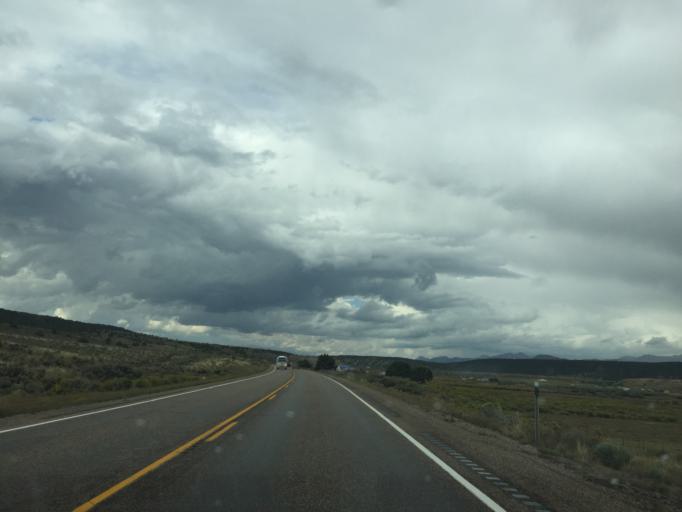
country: US
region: Utah
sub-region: Garfield County
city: Panguitch
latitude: 37.7336
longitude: -112.3797
